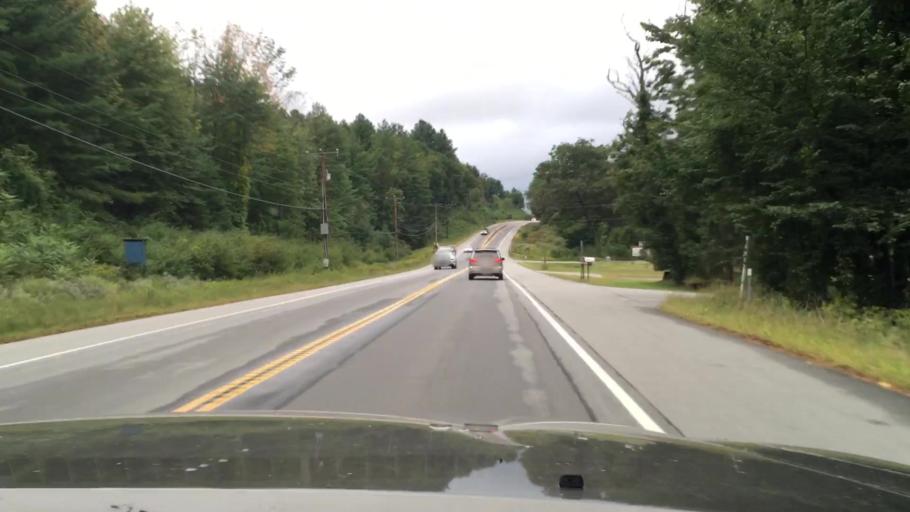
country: US
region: Vermont
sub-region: Windham County
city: Brattleboro
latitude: 42.8874
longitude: -72.5339
